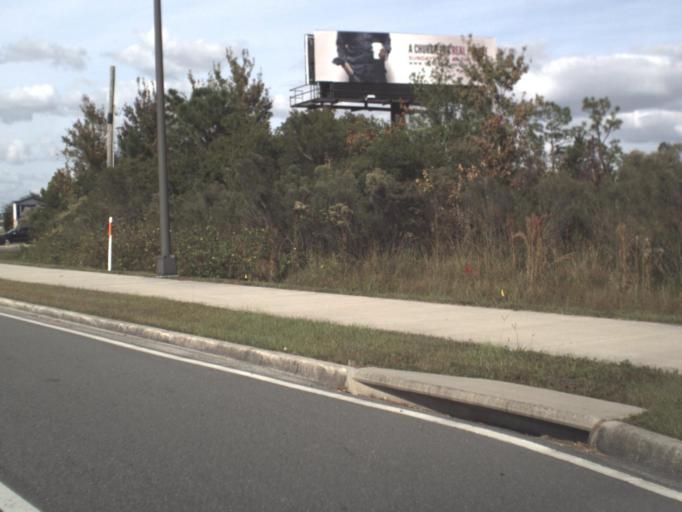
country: US
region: Florida
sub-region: Orange County
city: Hunters Creek
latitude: 28.3365
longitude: -81.4194
